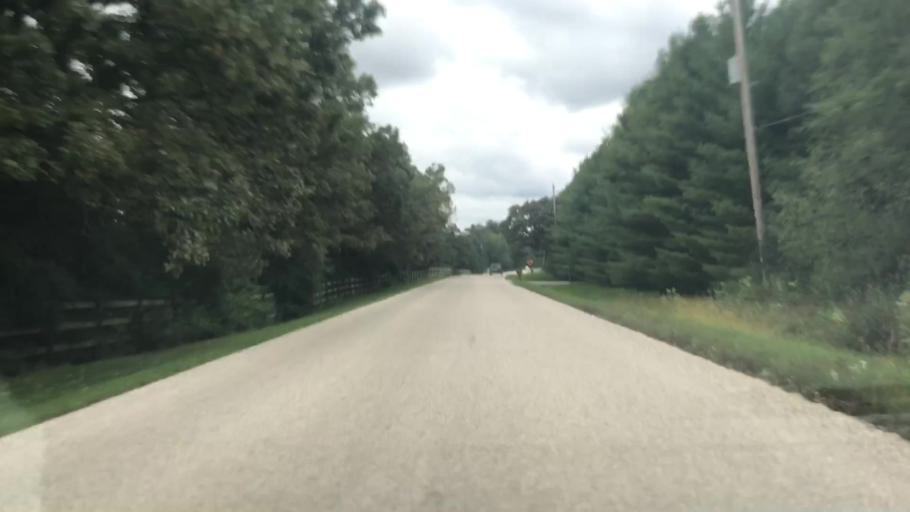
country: US
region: Wisconsin
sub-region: Waukesha County
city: North Prairie
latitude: 42.9183
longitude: -88.4351
